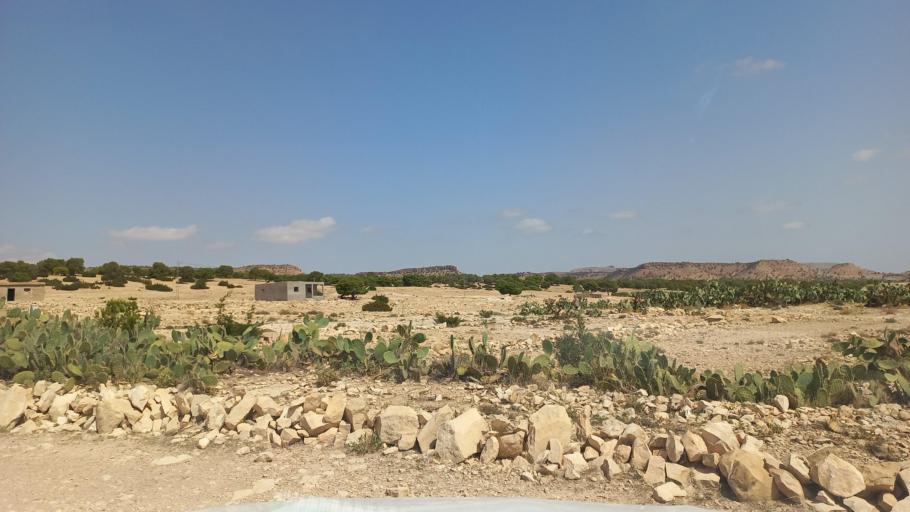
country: TN
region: Al Qasrayn
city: Sbiba
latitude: 35.4023
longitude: 8.9654
